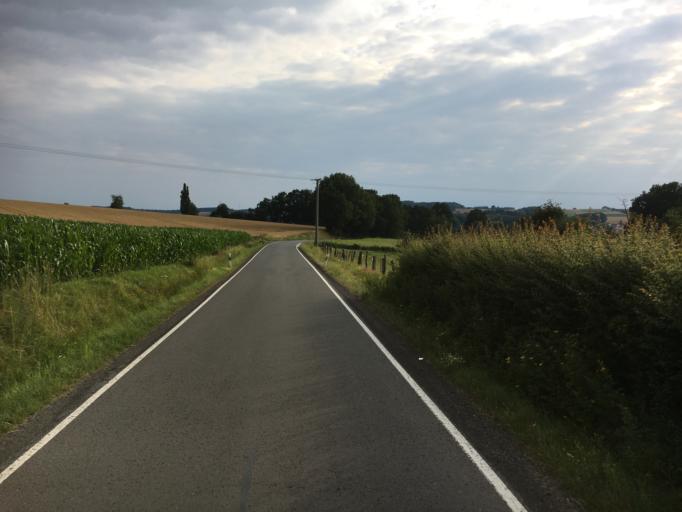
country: DE
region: Hesse
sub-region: Regierungsbezirk Kassel
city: Schrecksbach
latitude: 50.8529
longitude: 9.3010
